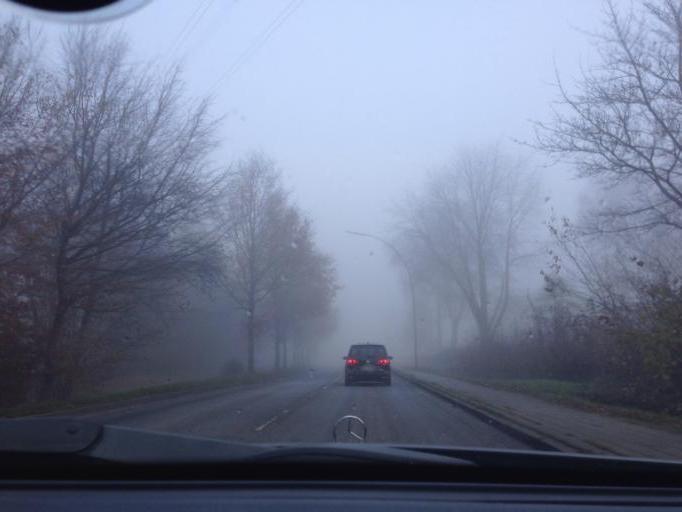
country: DE
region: Schleswig-Holstein
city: Stapelfeld
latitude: 53.6338
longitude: 10.1868
